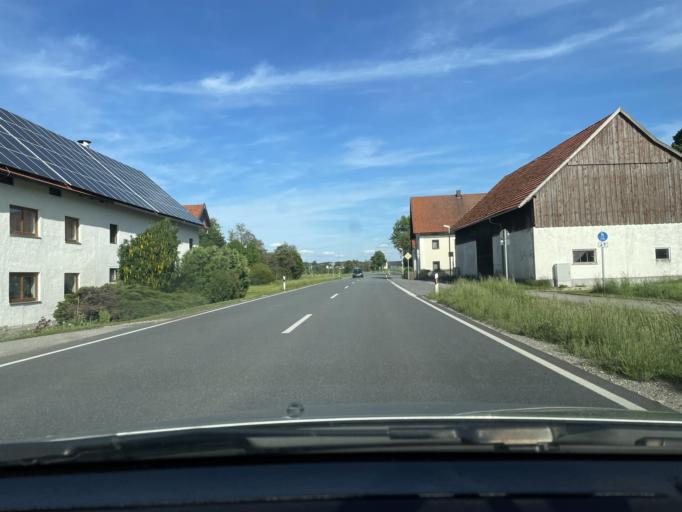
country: DE
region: Bavaria
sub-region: Lower Bavaria
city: Furth
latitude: 48.6092
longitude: 12.0184
